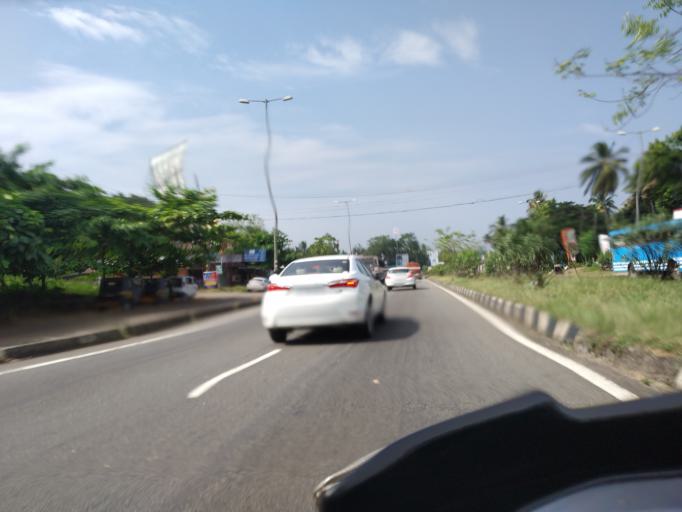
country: IN
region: Kerala
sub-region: Ernakulam
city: Angamali
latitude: 10.2447
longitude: 76.3717
